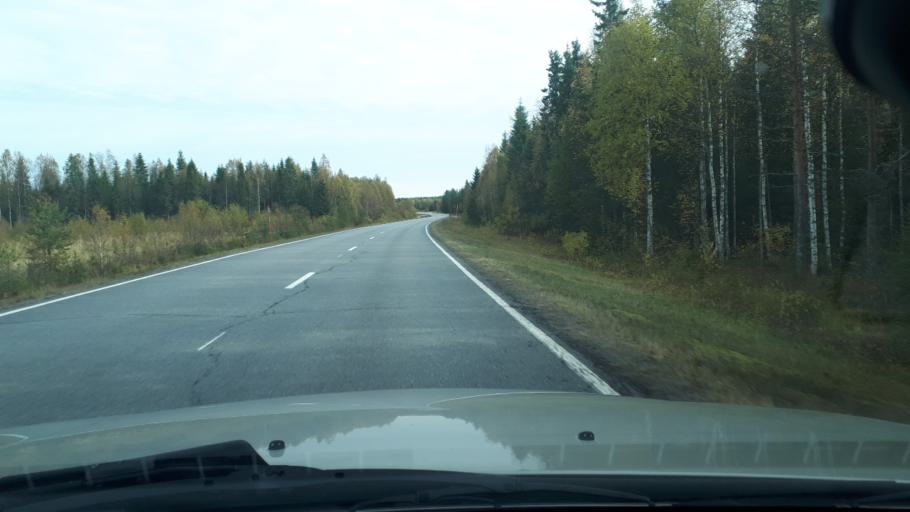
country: FI
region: Lapland
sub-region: Rovaniemi
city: Ranua
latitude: 65.9834
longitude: 26.1519
